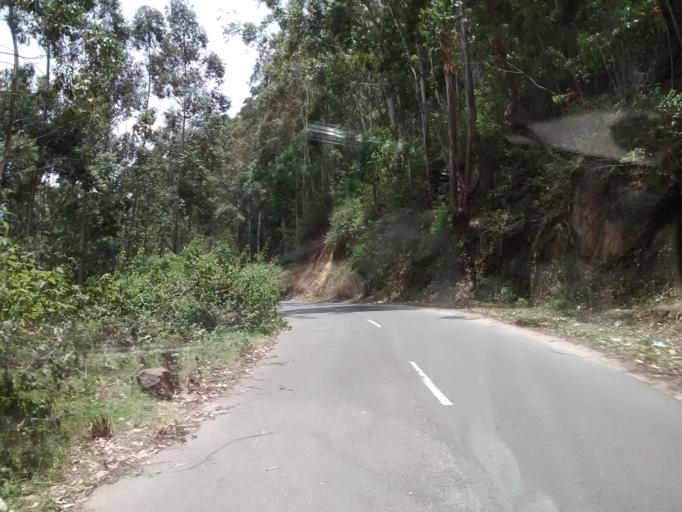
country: IN
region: Kerala
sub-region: Idukki
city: Munnar
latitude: 10.1377
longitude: 77.1885
